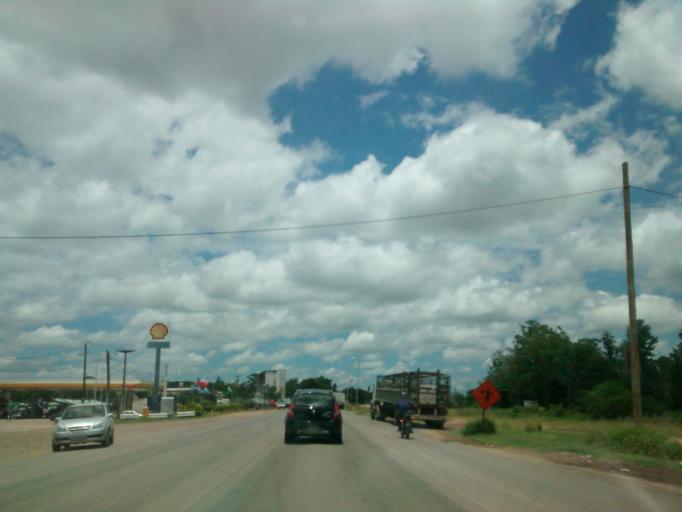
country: AR
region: Chaco
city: Fontana
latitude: -27.4151
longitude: -59.0034
